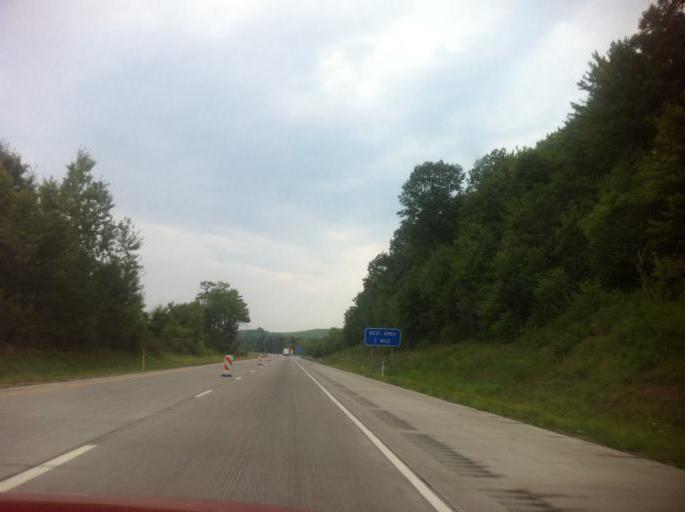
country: US
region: Pennsylvania
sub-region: Jefferson County
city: Reynoldsville
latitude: 41.1528
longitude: -78.9196
